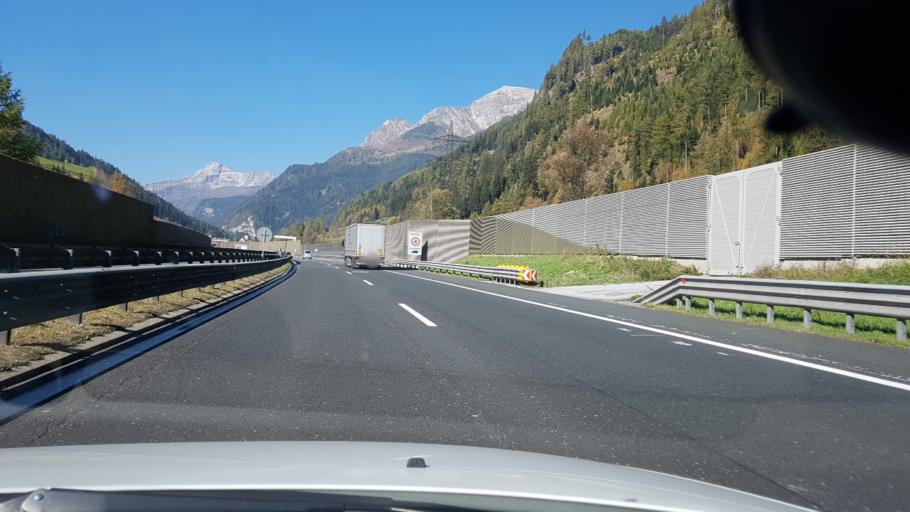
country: AT
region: Salzburg
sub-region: Politischer Bezirk Tamsweg
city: Zederhaus
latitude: 47.1452
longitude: 13.5211
